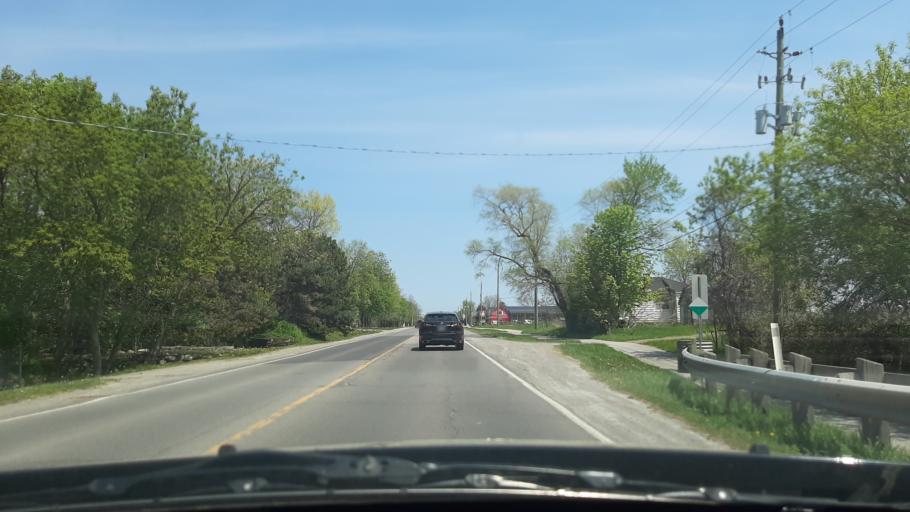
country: US
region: New York
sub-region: Niagara County
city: Youngstown
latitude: 43.2386
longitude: -79.1012
